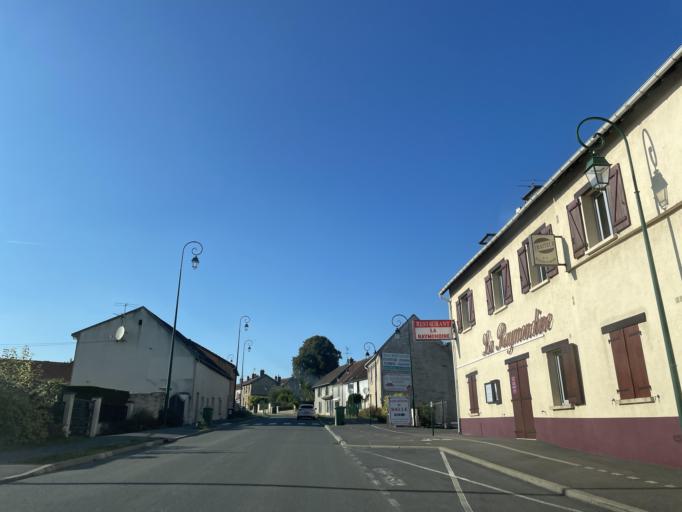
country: FR
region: Ile-de-France
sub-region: Departement de Seine-et-Marne
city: Mouroux
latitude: 48.8276
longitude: 3.0327
